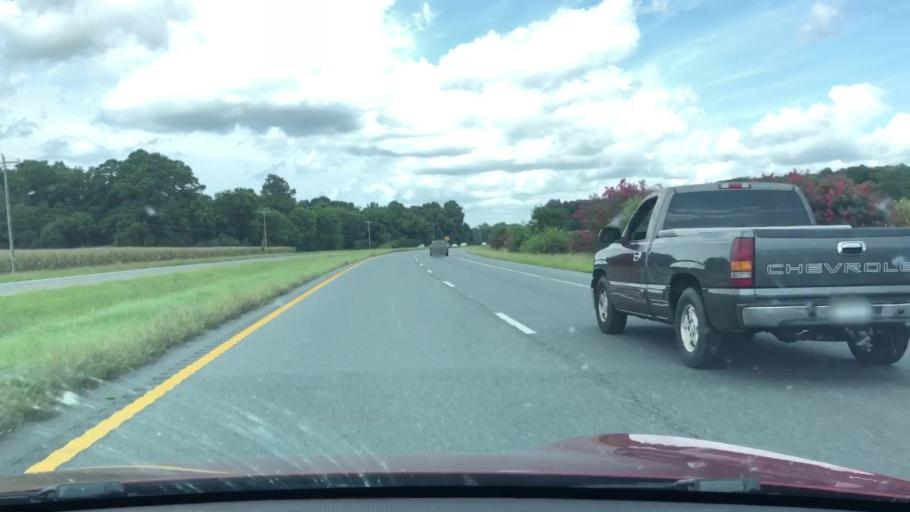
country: US
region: Virginia
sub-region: Northampton County
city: Cape Charles
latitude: 37.2836
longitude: -75.9796
